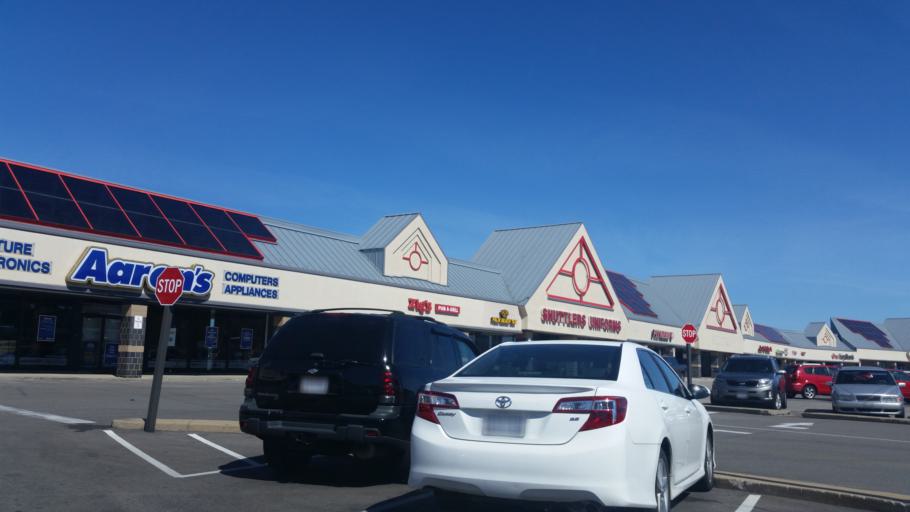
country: US
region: Ohio
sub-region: Cuyahoga County
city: Brooklyn Heights
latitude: 41.4058
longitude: -81.6969
